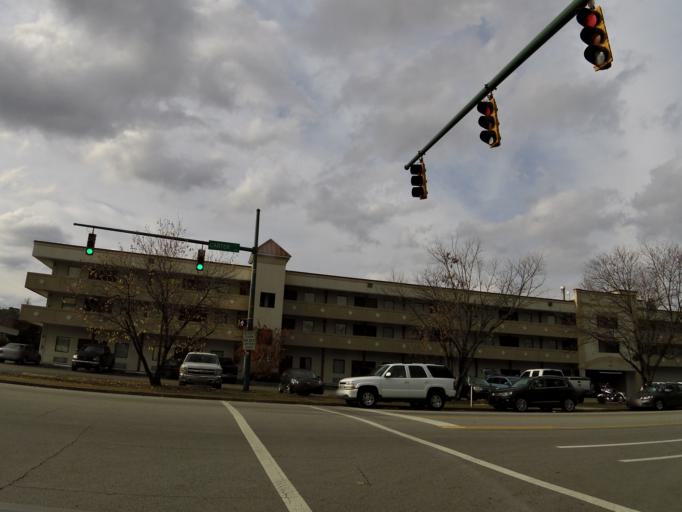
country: US
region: Tennessee
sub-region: Hamilton County
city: Chattanooga
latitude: 35.0450
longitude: -85.3119
